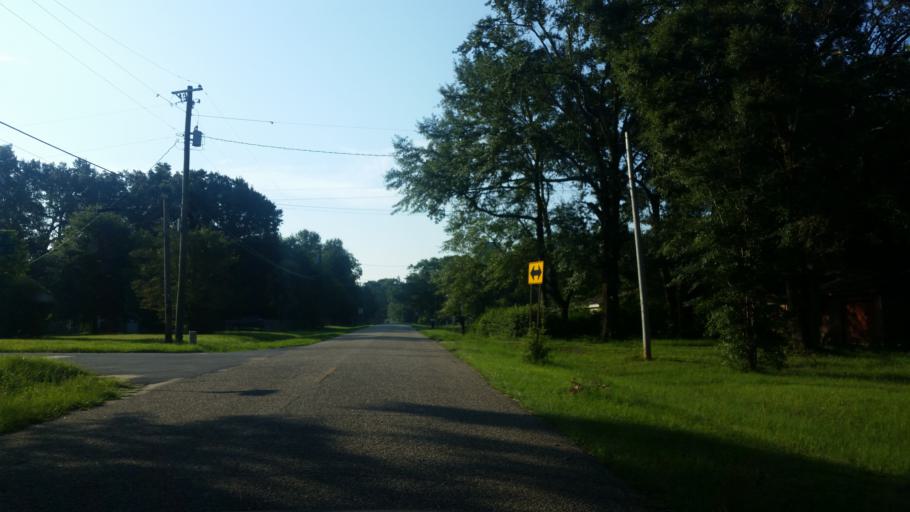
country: US
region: Florida
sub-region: Escambia County
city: Gonzalez
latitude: 30.5866
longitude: -87.2993
